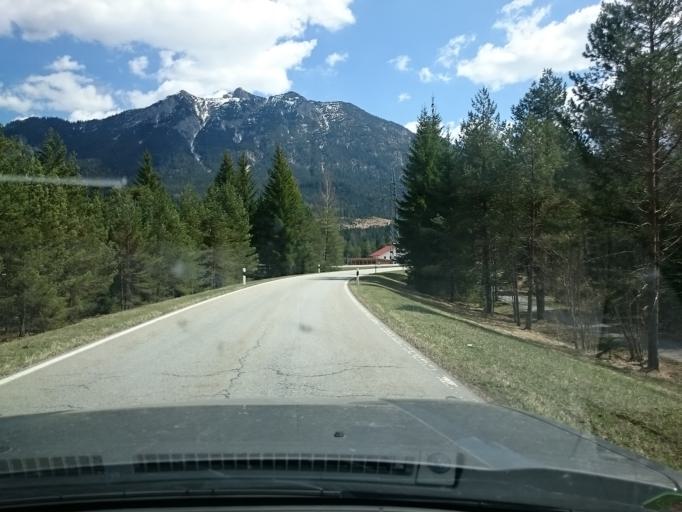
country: DE
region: Bavaria
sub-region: Upper Bavaria
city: Krun
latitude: 47.4964
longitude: 11.2734
